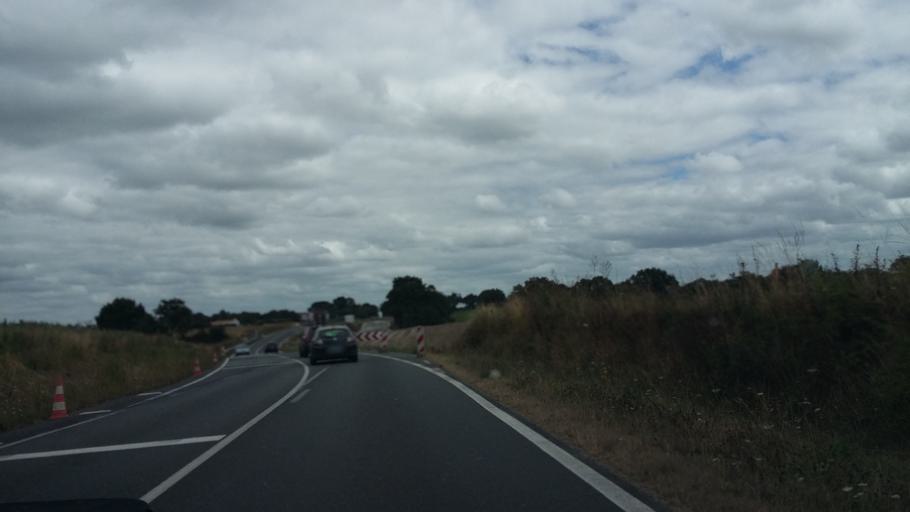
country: FR
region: Pays de la Loire
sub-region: Departement de la Vendee
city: Saint-Christophe-du-Ligneron
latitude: 46.8255
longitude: -1.7860
